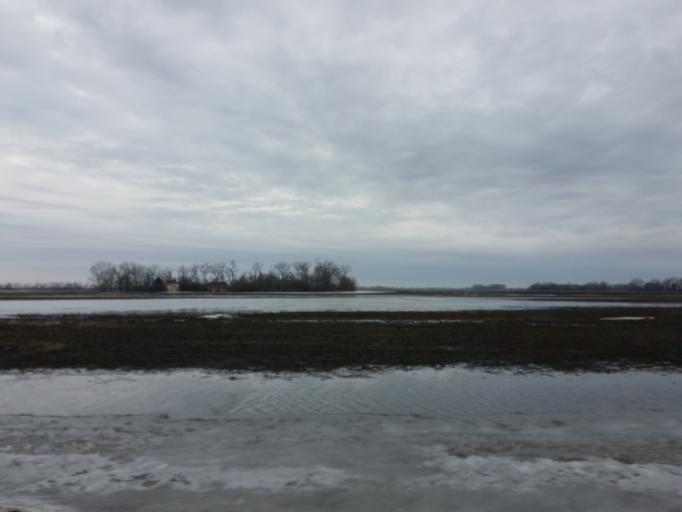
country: US
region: North Dakota
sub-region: Walsh County
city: Grafton
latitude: 48.3854
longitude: -97.4704
